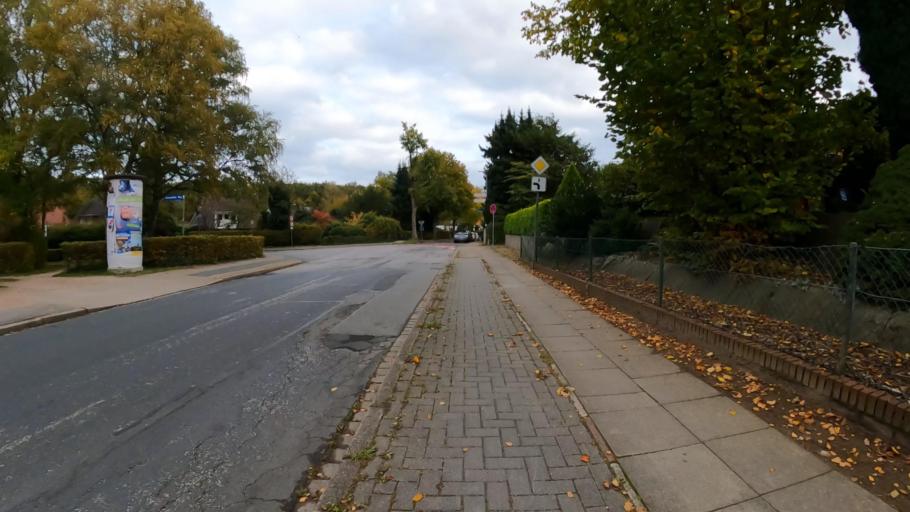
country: DE
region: Schleswig-Holstein
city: Ahrensburg
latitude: 53.6579
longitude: 10.2420
